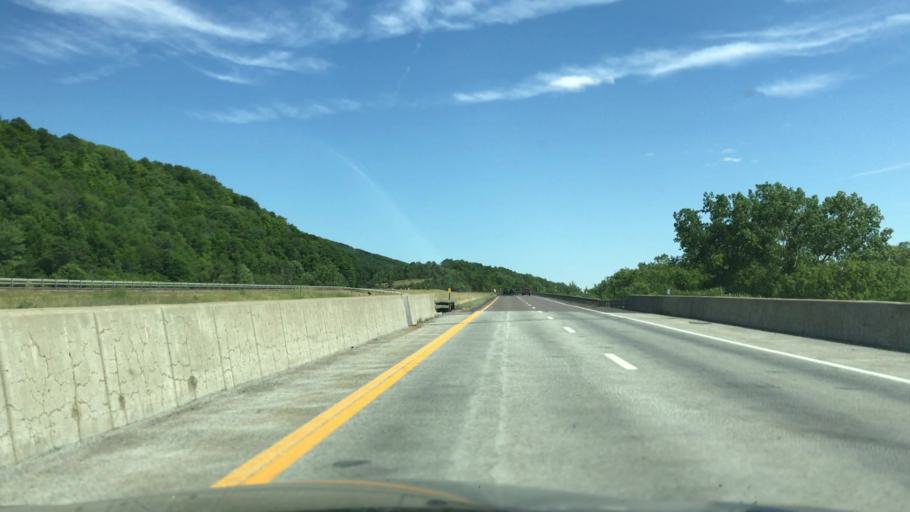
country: US
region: New York
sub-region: Steuben County
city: Bath
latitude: 42.4206
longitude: -77.4265
